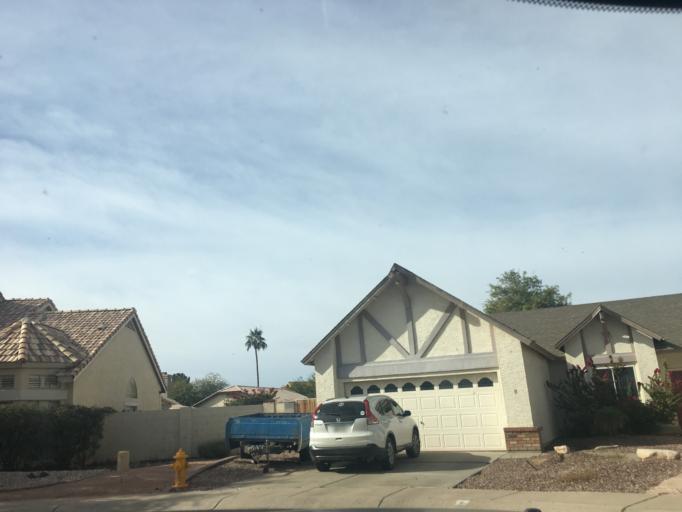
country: US
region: Arizona
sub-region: Maricopa County
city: Gilbert
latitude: 33.3494
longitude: -111.8032
